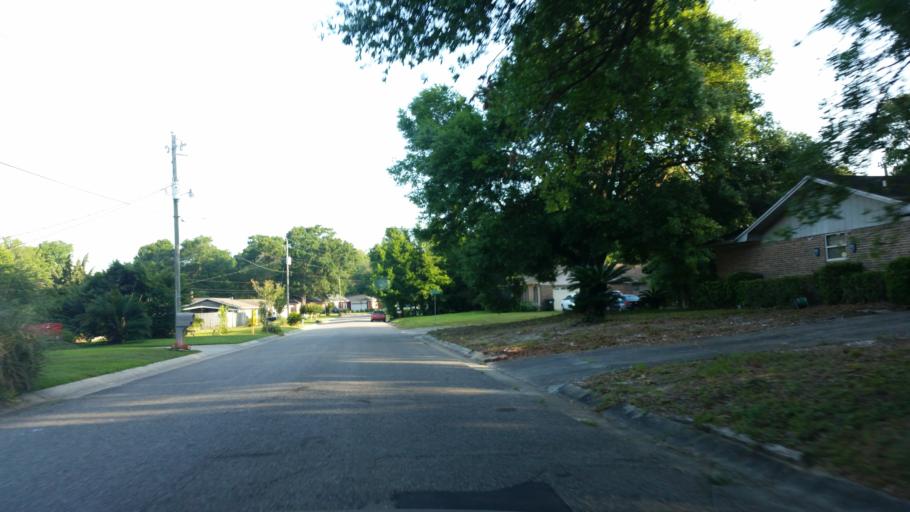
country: US
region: Florida
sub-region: Escambia County
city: Ferry Pass
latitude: 30.5068
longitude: -87.2020
